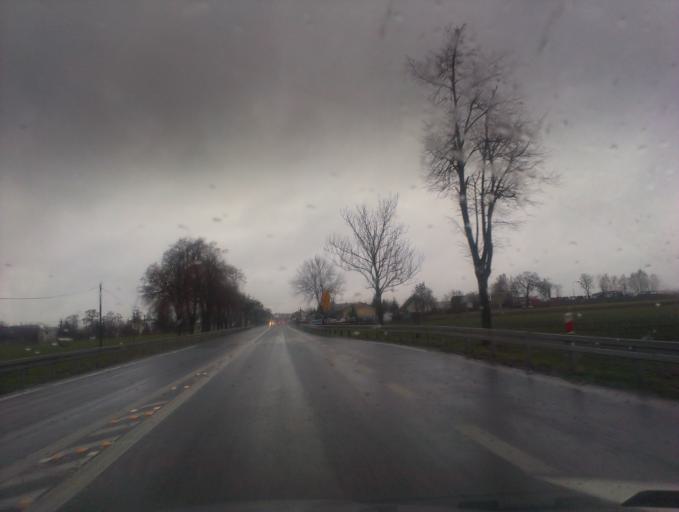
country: PL
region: Greater Poland Voivodeship
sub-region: Powiat obornicki
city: Oborniki
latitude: 52.6199
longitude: 16.8117
